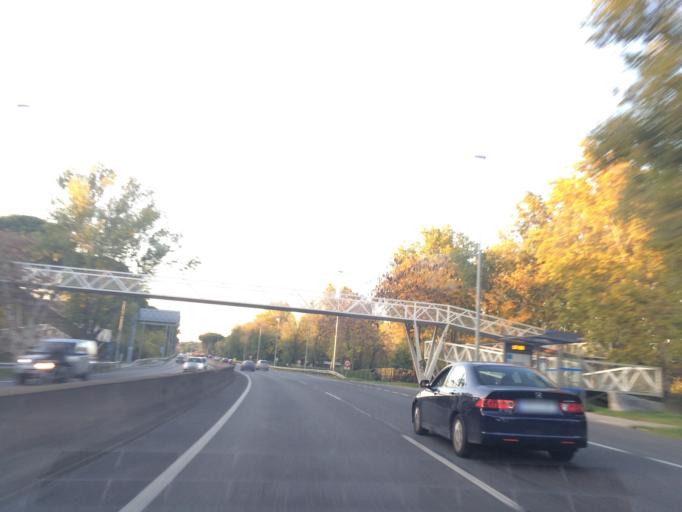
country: ES
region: Madrid
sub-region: Provincia de Madrid
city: Moncloa-Aravaca
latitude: 40.4373
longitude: -3.7413
